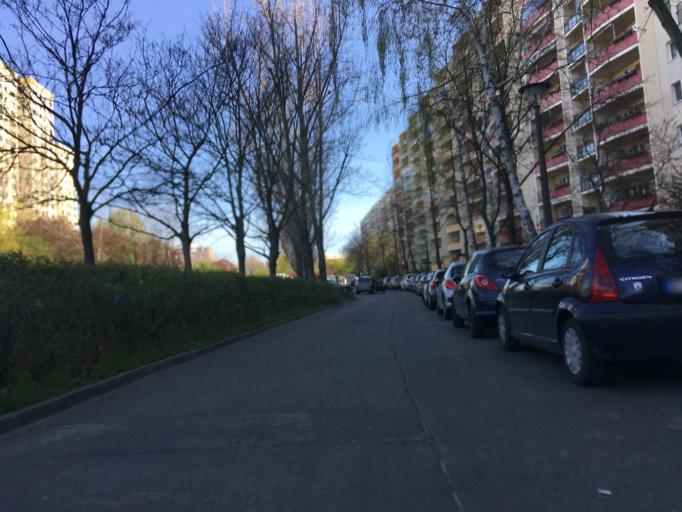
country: DE
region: Berlin
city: Marzahn
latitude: 52.5527
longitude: 13.5653
